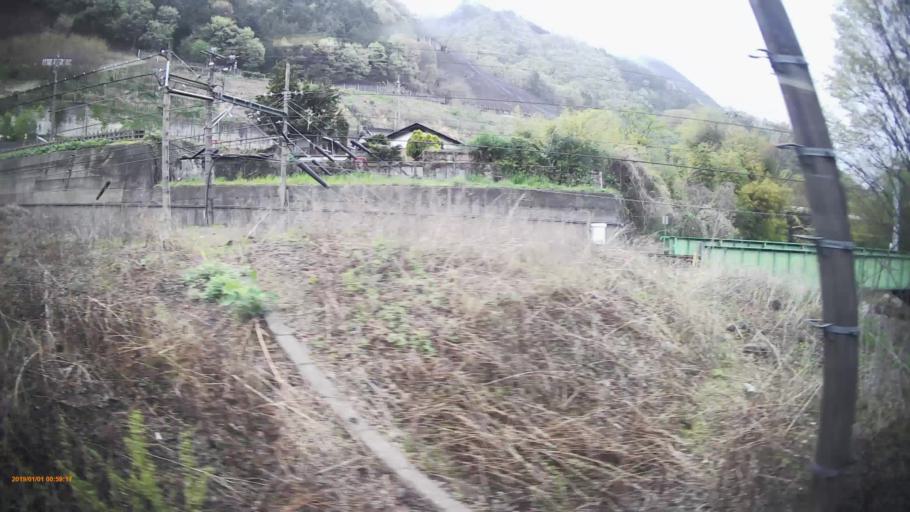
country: JP
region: Yamanashi
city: Otsuki
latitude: 35.6053
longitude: 138.8177
